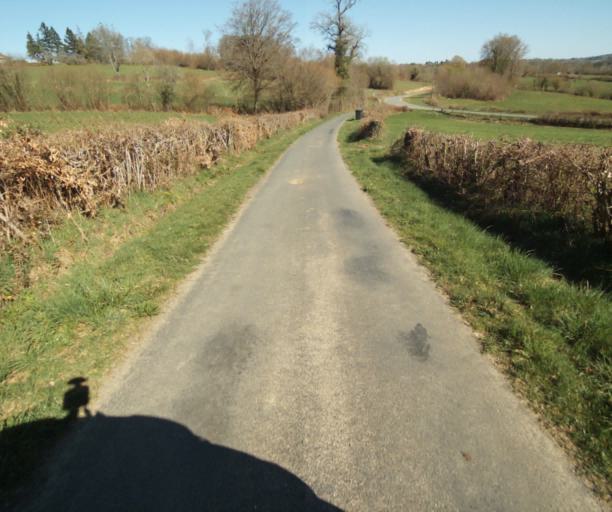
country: FR
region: Limousin
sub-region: Departement de la Correze
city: Chamboulive
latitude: 45.4252
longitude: 1.6405
